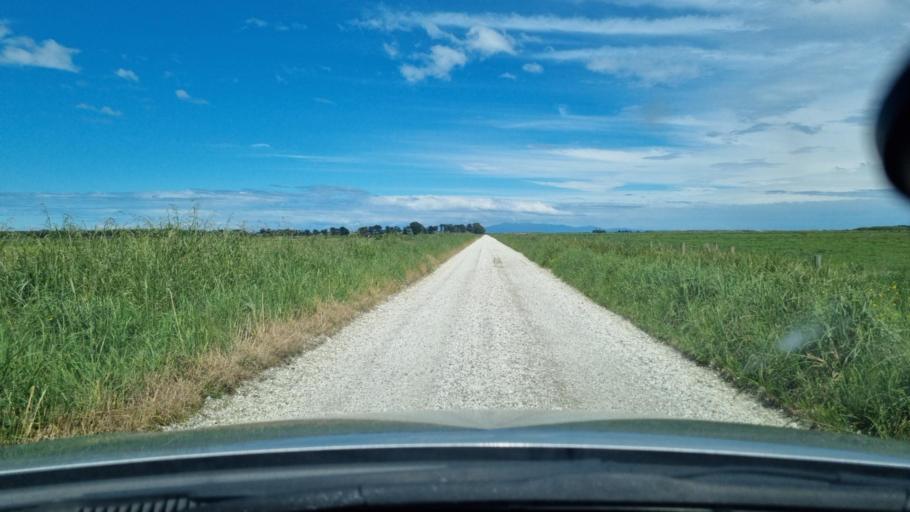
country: NZ
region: Southland
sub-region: Invercargill City
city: Invercargill
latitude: -46.3756
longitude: 168.2743
